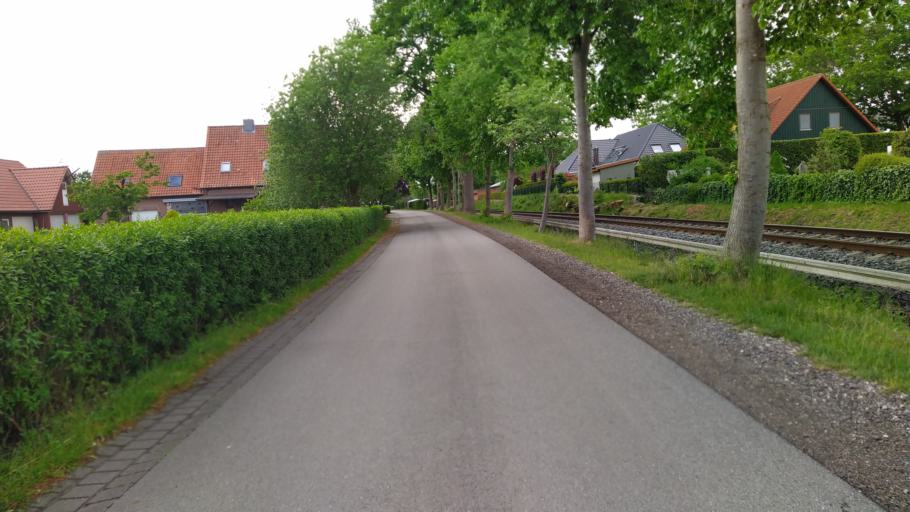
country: DE
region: Lower Saxony
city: Bargstedt
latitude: 53.4580
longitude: 9.4401
